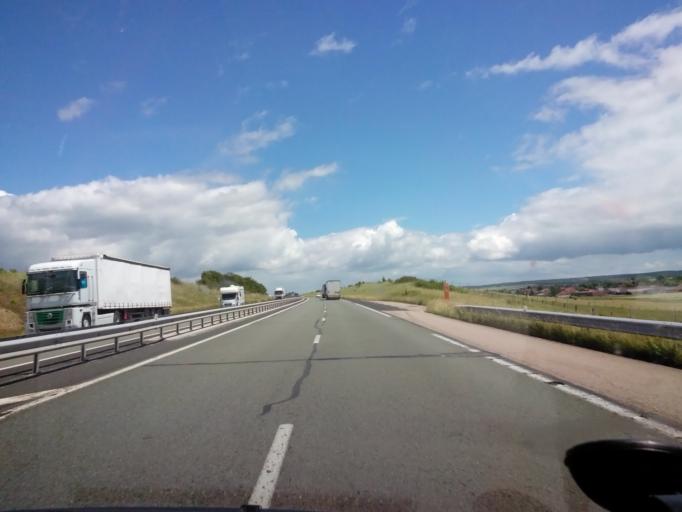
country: FR
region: Lorraine
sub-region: Departement des Vosges
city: Bulgneville
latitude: 48.1811
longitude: 5.7455
